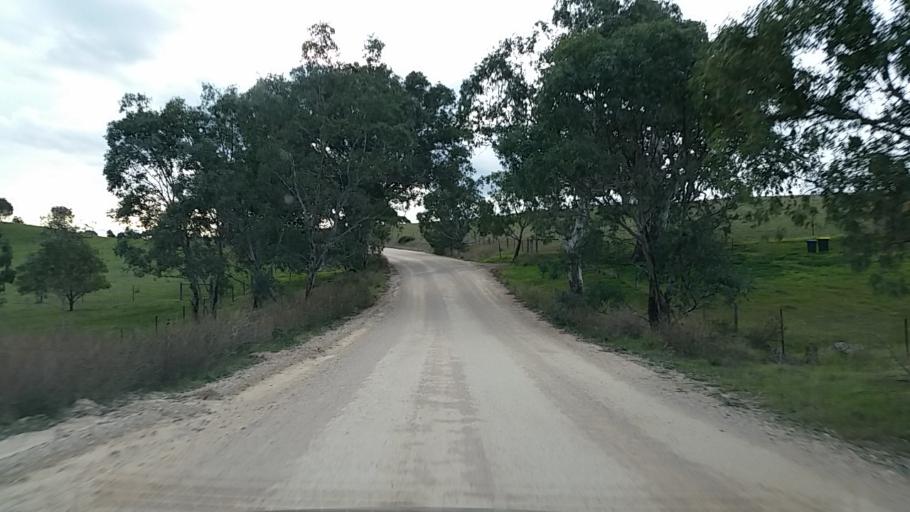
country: AU
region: South Australia
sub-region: Mount Barker
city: Callington
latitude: -34.9917
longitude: 139.0394
